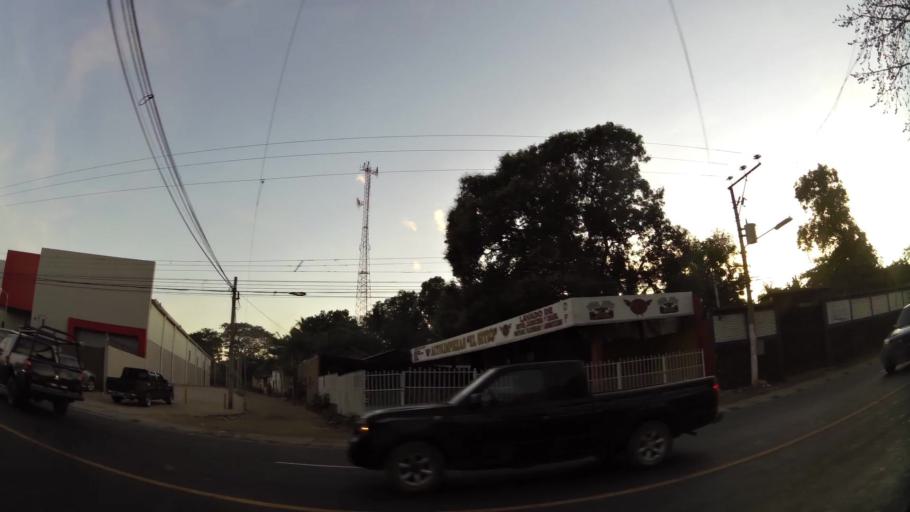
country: SV
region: San Miguel
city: San Miguel
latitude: 13.4975
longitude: -88.2053
